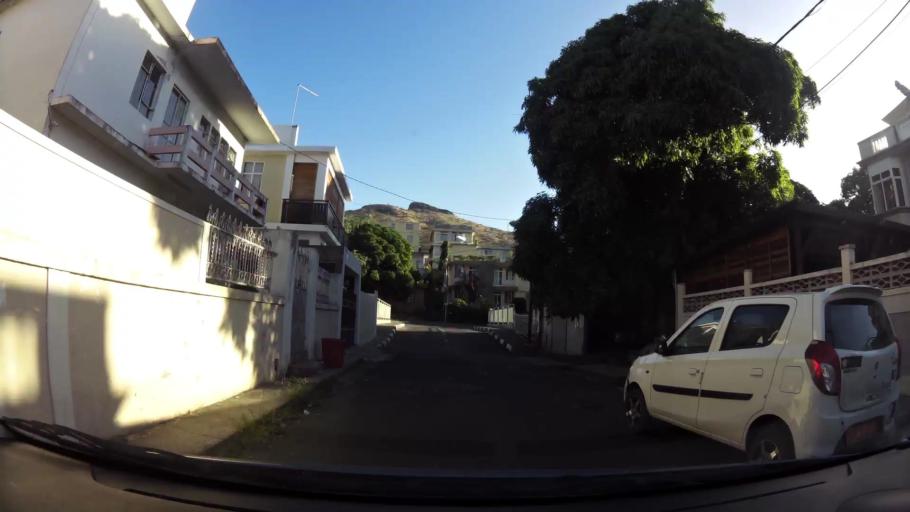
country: MU
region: Port Louis
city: Port Louis
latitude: -20.1708
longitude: 57.5067
